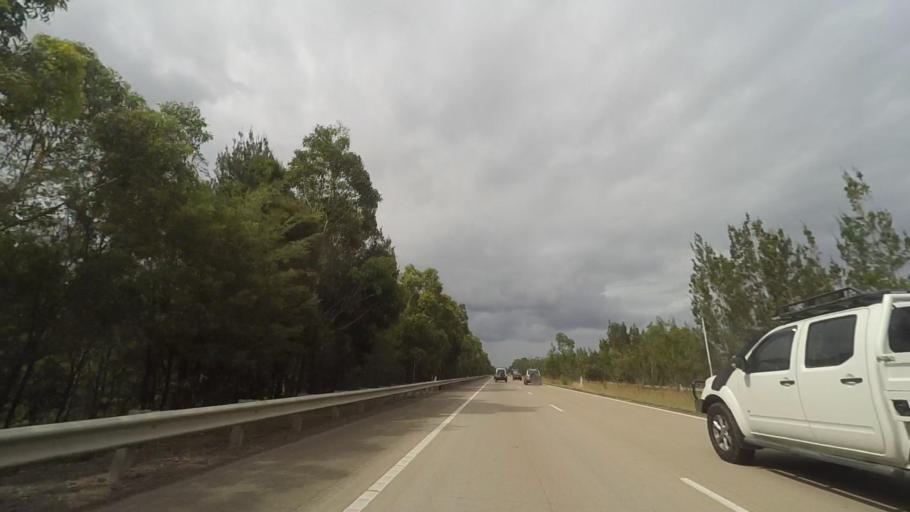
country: AU
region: New South Wales
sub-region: Port Stephens Shire
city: Raymond Terrace
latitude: -32.7284
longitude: 151.7844
